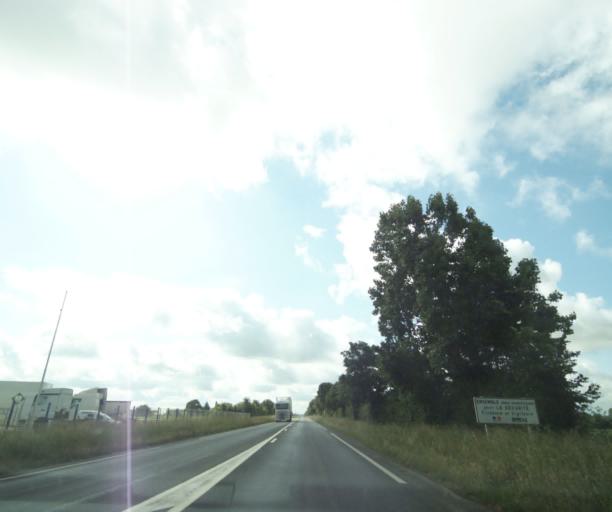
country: FR
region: Pays de la Loire
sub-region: Departement de la Sarthe
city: Solesmes
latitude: 47.8202
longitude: -0.2967
